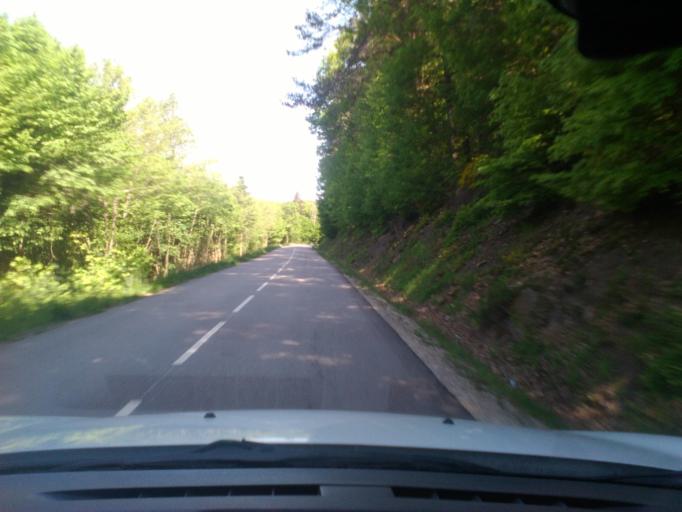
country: FR
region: Lorraine
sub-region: Departement des Vosges
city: Bruyeres
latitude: 48.2627
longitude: 6.7258
